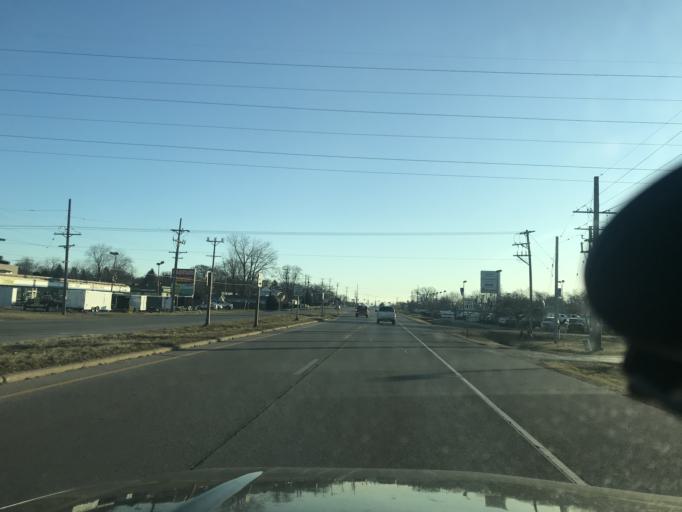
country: US
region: Wisconsin
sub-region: Kenosha County
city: Kenosha
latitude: 42.5664
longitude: -87.8757
